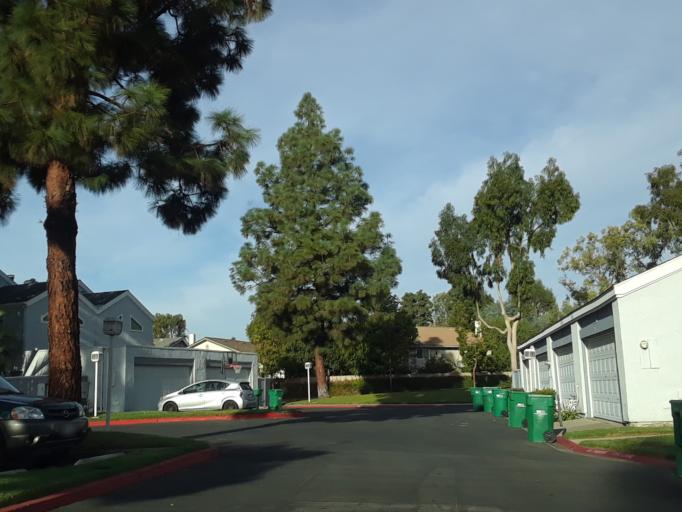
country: US
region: California
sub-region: Orange County
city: North Tustin
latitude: 33.7174
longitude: -117.7641
